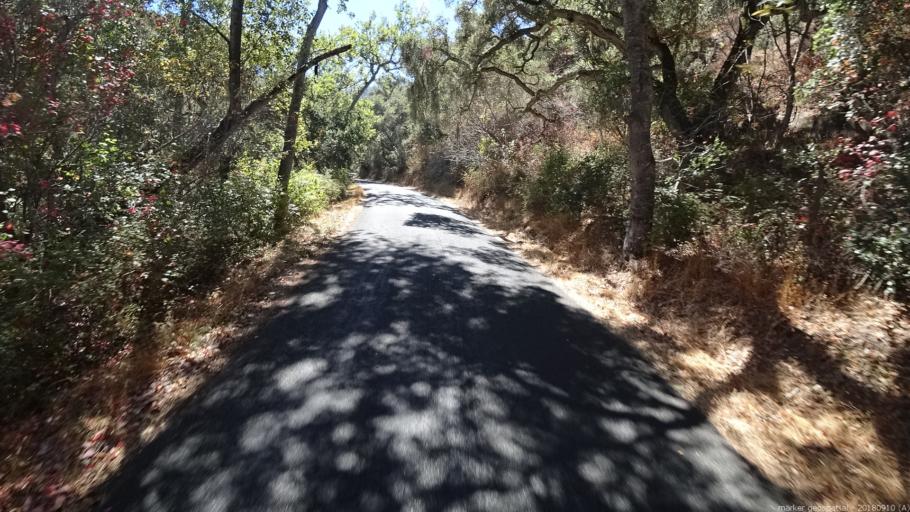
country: US
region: California
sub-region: Monterey County
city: Carmel Valley Village
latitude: 36.4875
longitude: -121.8102
